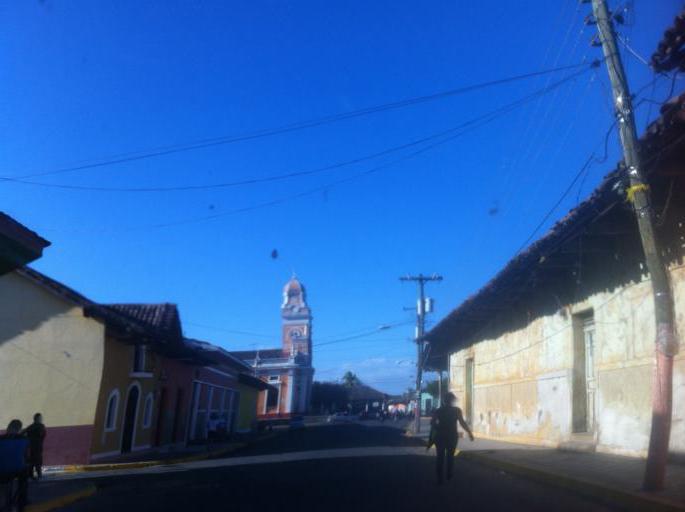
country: NI
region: Granada
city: Granada
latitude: 11.9278
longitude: -85.9605
